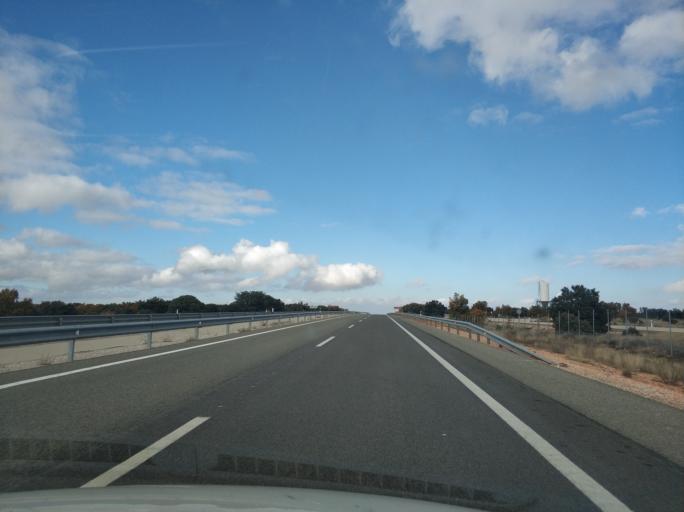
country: ES
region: Castille and Leon
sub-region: Provincia de Soria
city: Adradas
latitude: 41.3020
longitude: -2.4791
